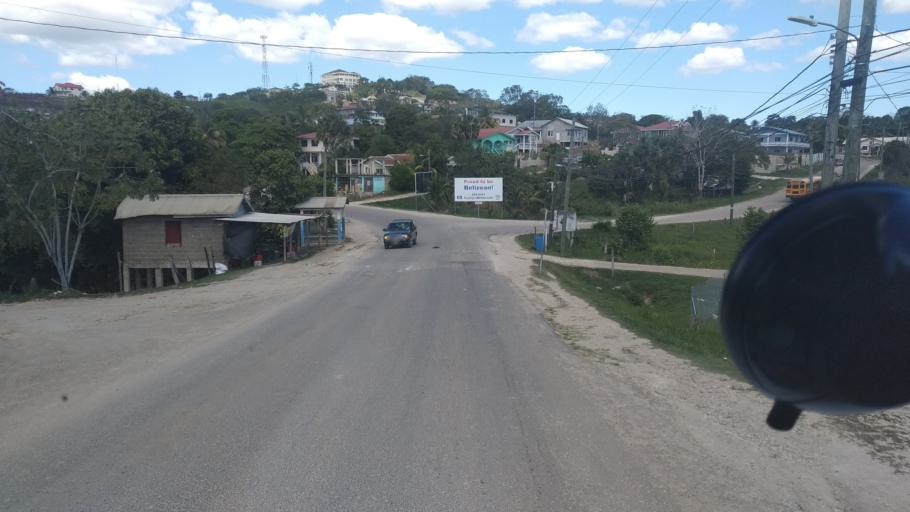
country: BZ
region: Cayo
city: Benque Viejo del Carmen
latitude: 17.0750
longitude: -89.1347
